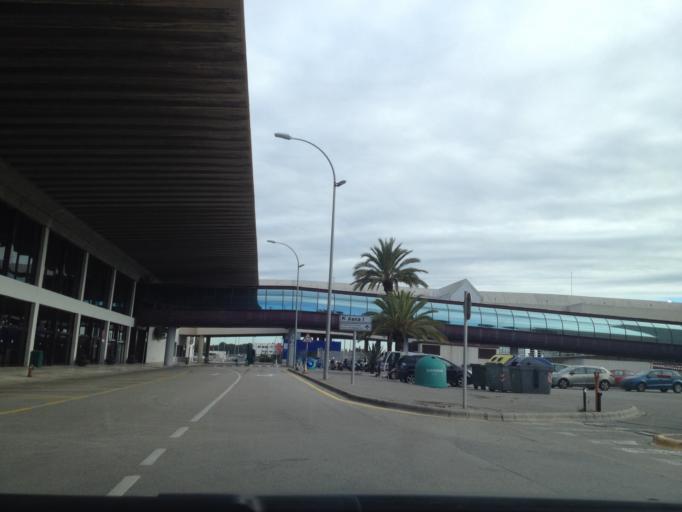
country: ES
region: Balearic Islands
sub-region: Illes Balears
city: s'Arenal
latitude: 39.5498
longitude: 2.7294
